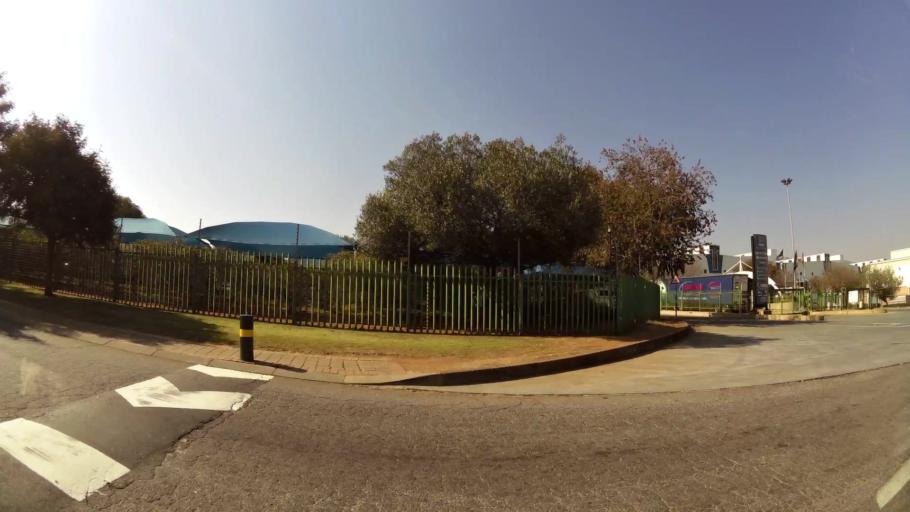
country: ZA
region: Gauteng
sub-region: City of Johannesburg Metropolitan Municipality
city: Modderfontein
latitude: -26.1082
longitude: 28.1330
